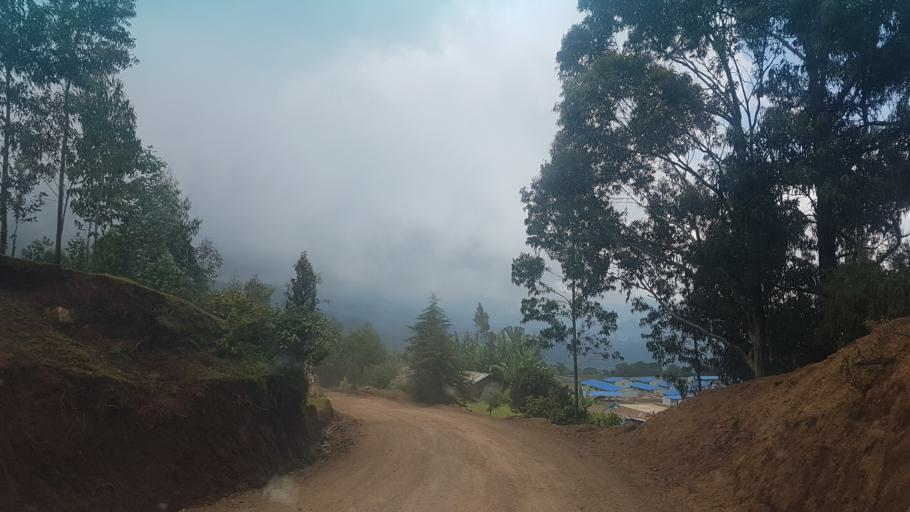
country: ET
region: Southern Nations, Nationalities, and People's Region
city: Arba Minch'
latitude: 6.3224
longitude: 37.5382
